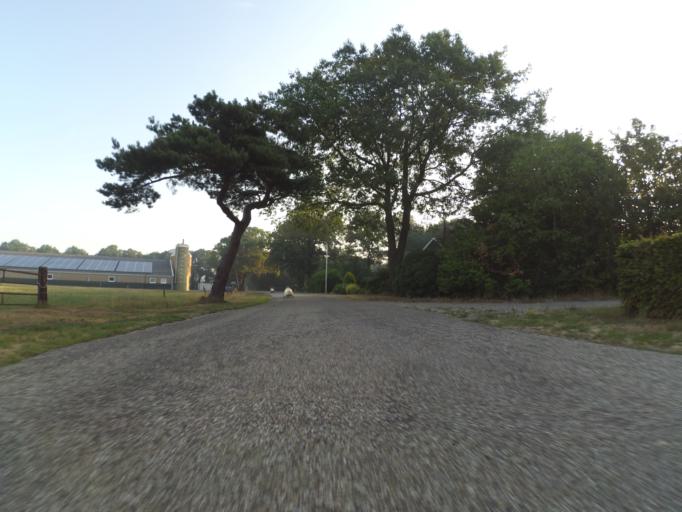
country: NL
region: Overijssel
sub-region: Gemeente Twenterand
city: Magele
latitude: 52.4254
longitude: 6.5316
